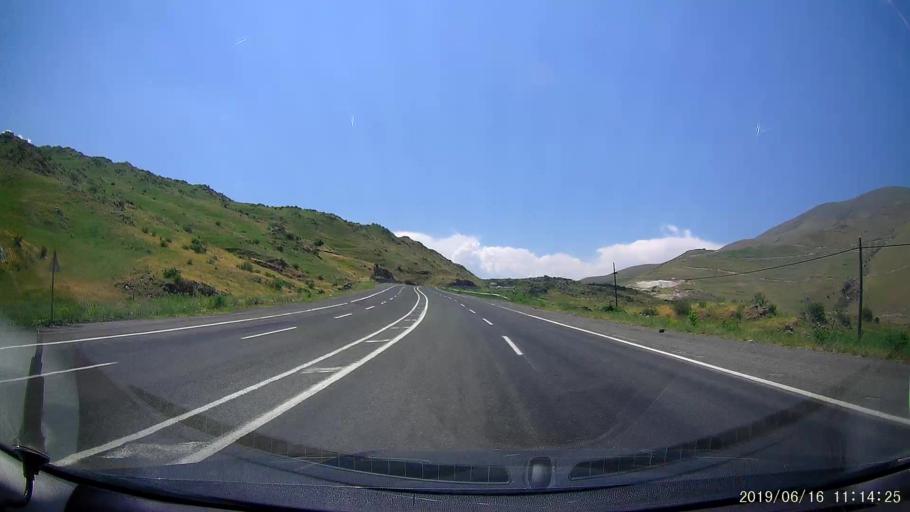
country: TR
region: Igdir
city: Igdir
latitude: 39.7794
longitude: 44.1422
